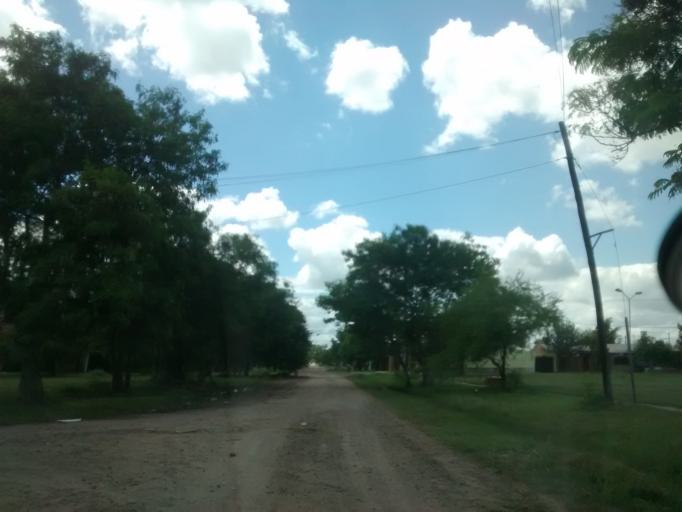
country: AR
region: Chaco
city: Resistencia
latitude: -27.4638
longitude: -59.0129
